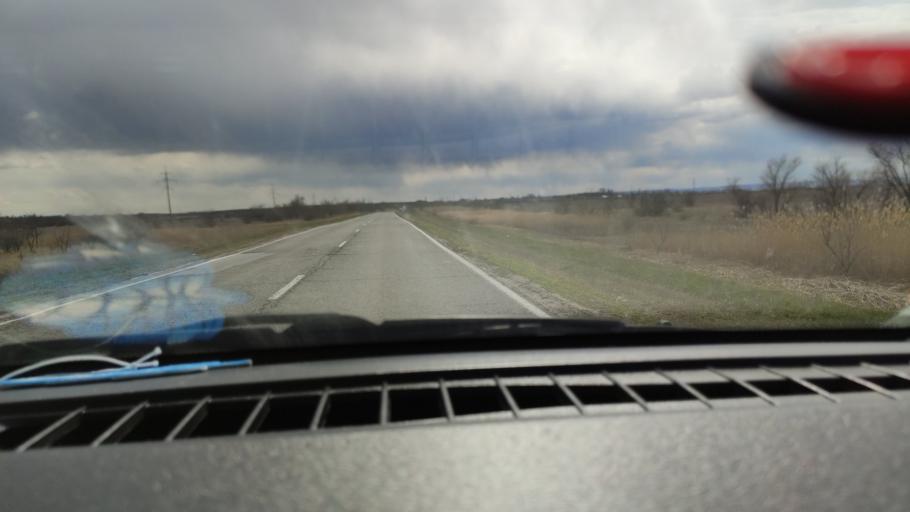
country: RU
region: Saratov
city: Privolzhskiy
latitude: 51.3081
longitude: 46.0101
